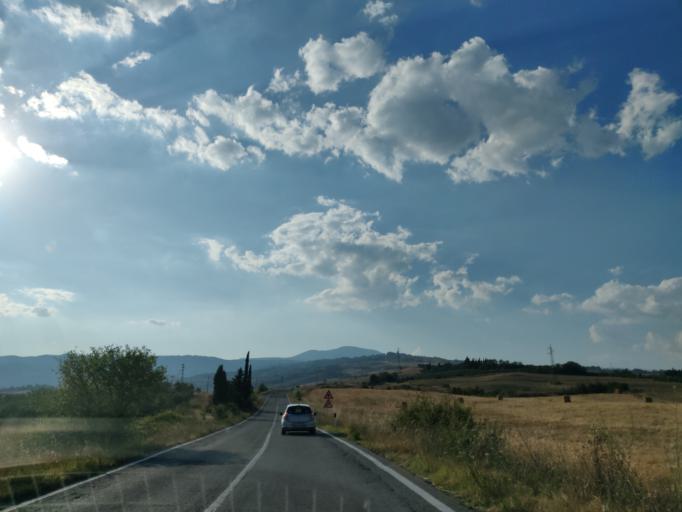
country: IT
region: Tuscany
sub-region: Provincia di Siena
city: Piancastagnaio
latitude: 42.8263
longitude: 11.7233
